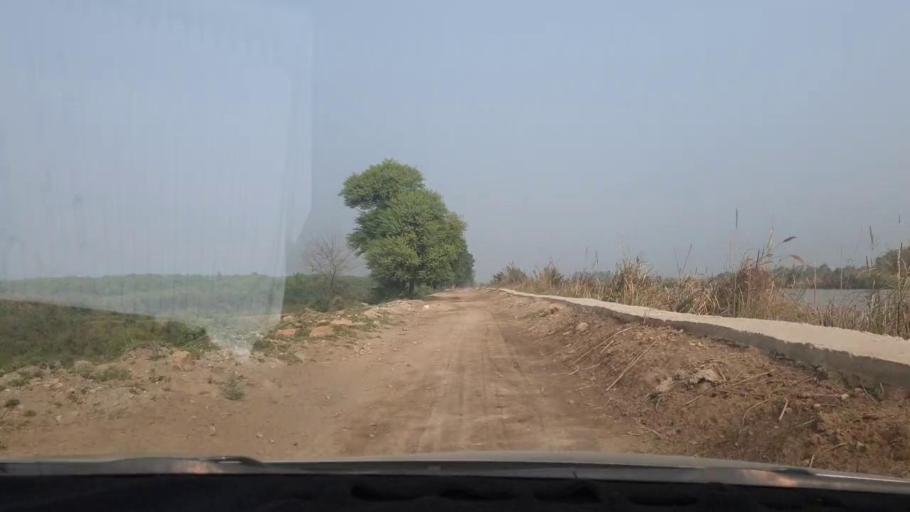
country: PK
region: Sindh
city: Matiari
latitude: 25.6698
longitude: 68.5585
